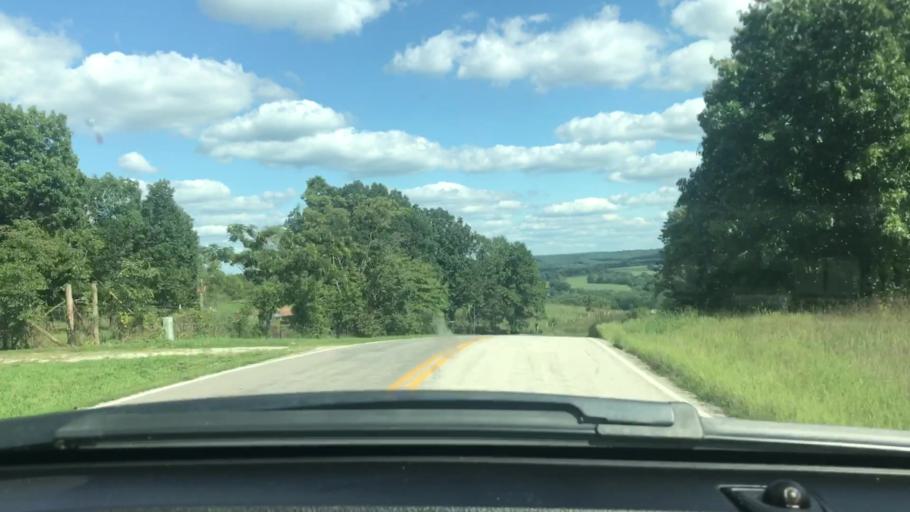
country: US
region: Missouri
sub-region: Wright County
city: Hartville
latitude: 37.3767
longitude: -92.4079
